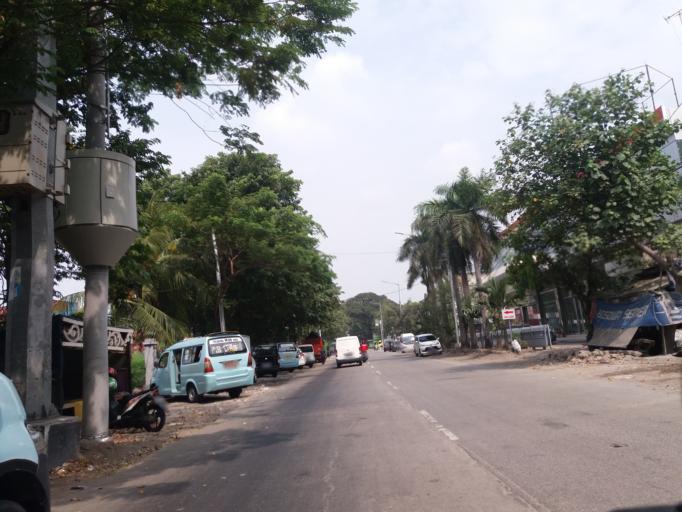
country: ID
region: Jakarta Raya
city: Jakarta
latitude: -6.1328
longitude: 106.8172
